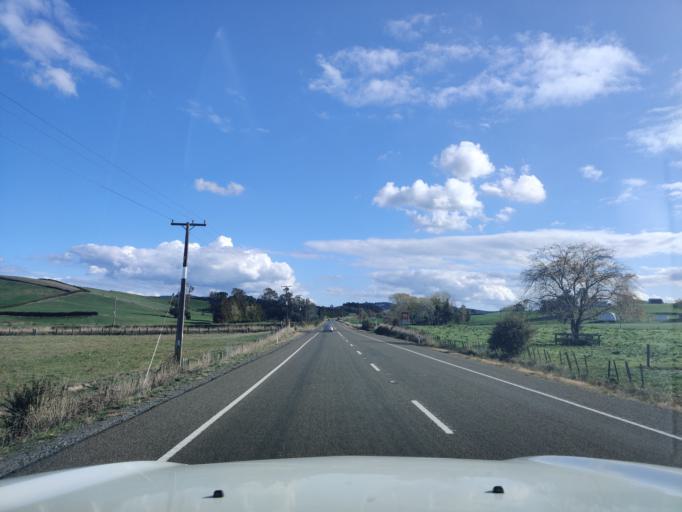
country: NZ
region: Waikato
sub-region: Hauraki District
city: Ngatea
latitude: -37.2865
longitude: 175.3915
